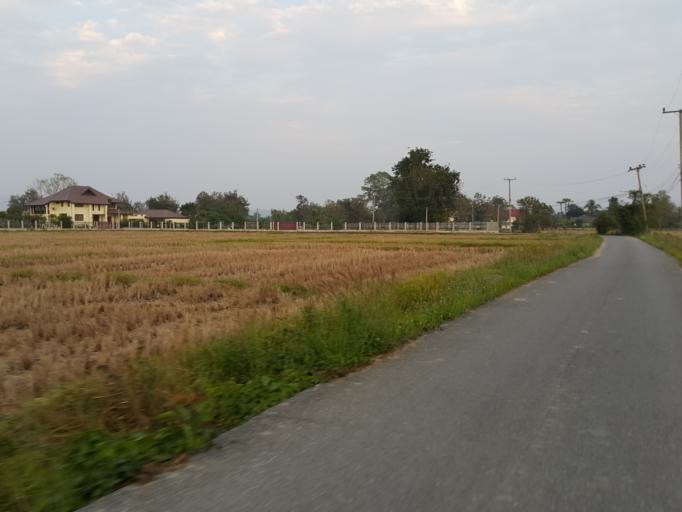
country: TH
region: Chiang Mai
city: San Sai
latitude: 18.8414
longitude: 99.1065
